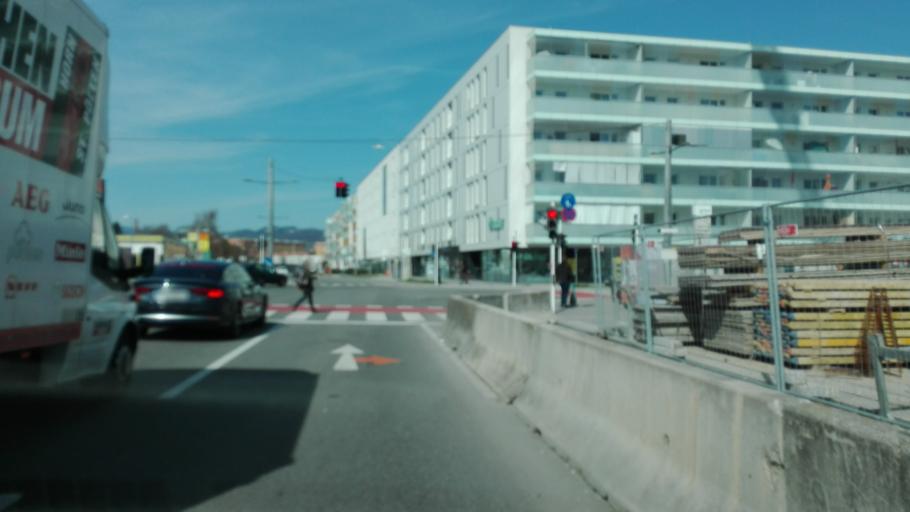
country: AT
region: Upper Austria
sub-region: Linz Stadt
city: Linz
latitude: 48.2922
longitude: 14.3057
